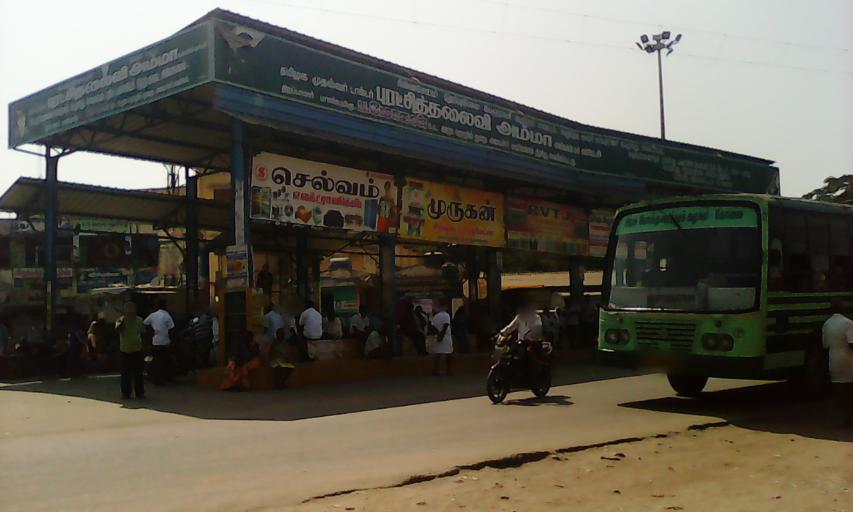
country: IN
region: Tamil Nadu
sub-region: Villupuram
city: Chinna Salem
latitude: 11.6355
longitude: 78.8775
